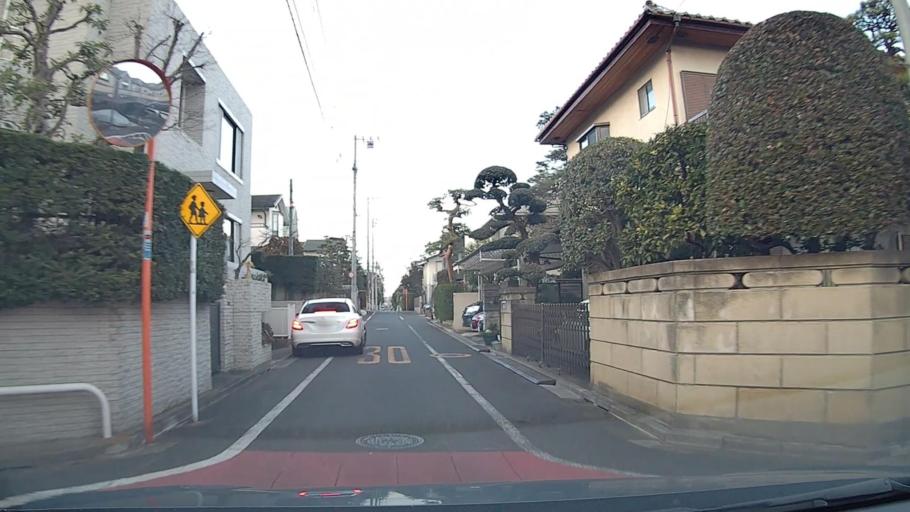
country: JP
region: Saitama
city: Asaka
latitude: 35.7693
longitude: 139.5841
